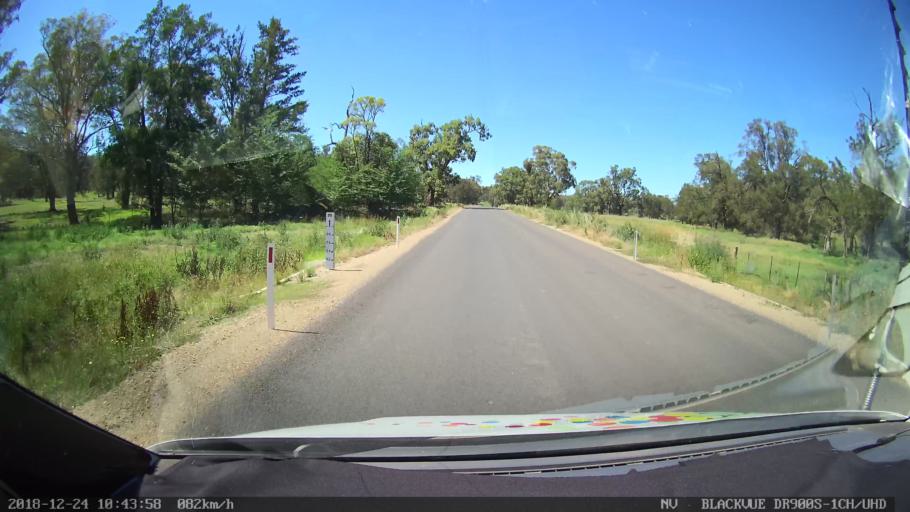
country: AU
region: New South Wales
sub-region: Upper Hunter Shire
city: Merriwa
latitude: -31.8875
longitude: 150.4438
